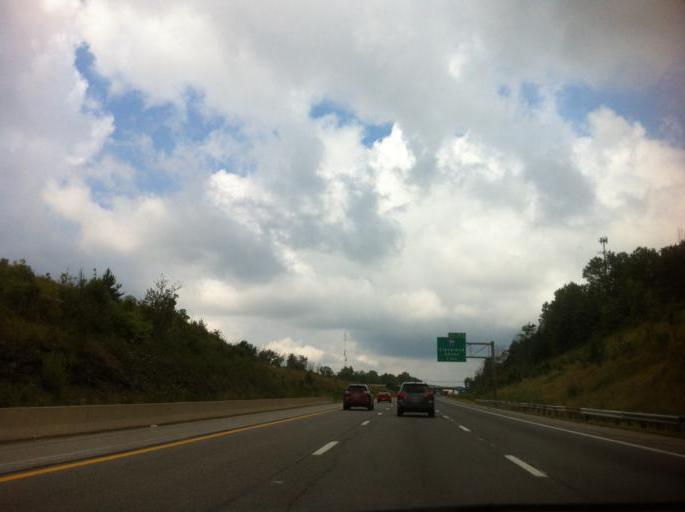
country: US
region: Ohio
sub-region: Summit County
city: Richfield
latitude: 41.2589
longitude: -81.6034
